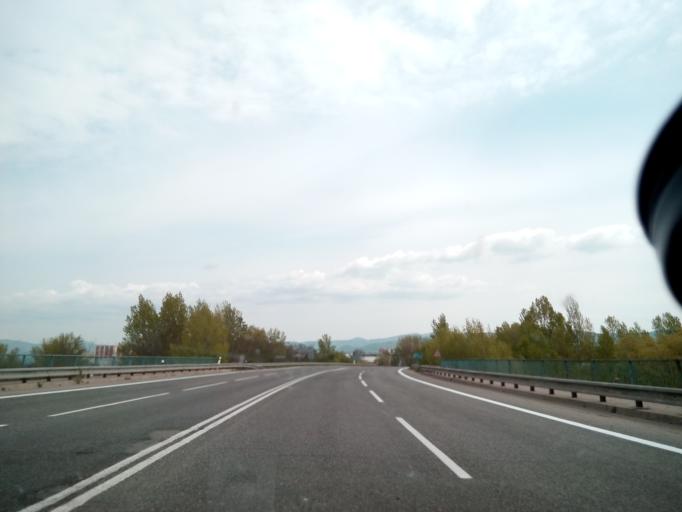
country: SK
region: Trnavsky
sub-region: Okres Trnava
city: Piestany
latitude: 48.5908
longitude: 17.7898
